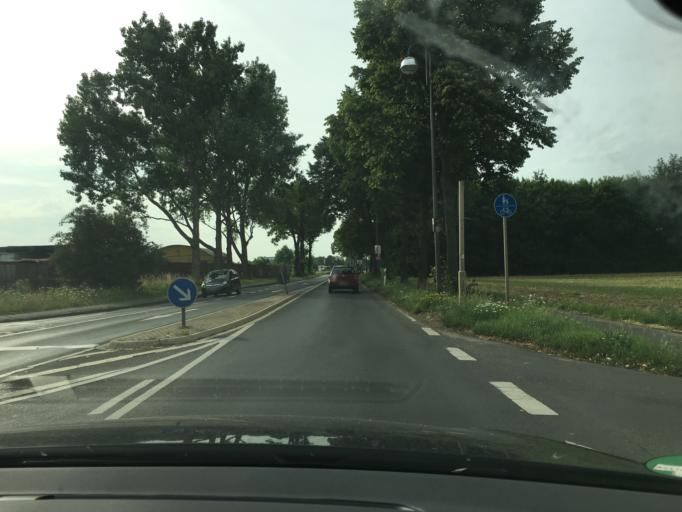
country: DE
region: North Rhine-Westphalia
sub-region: Regierungsbezirk Koln
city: Bonn
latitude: 50.7591
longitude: 7.0629
